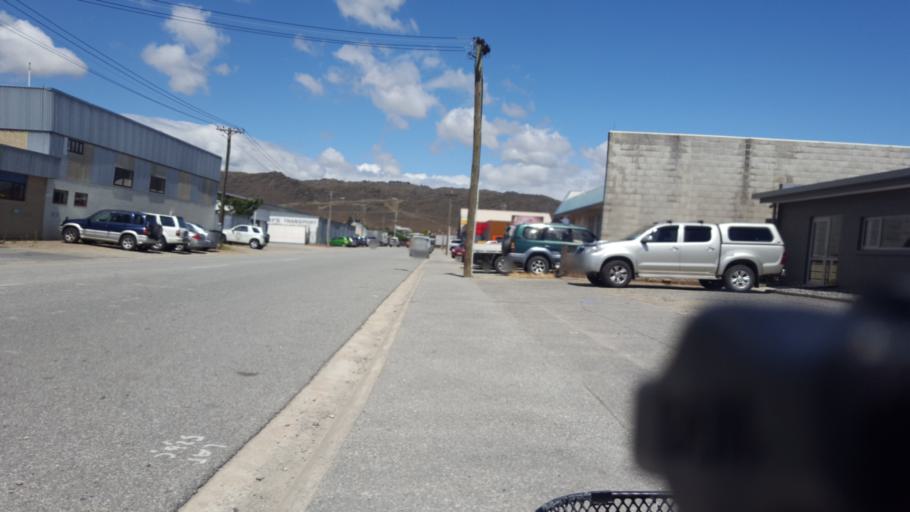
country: NZ
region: Otago
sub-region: Queenstown-Lakes District
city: Wanaka
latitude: -45.2448
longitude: 169.3927
